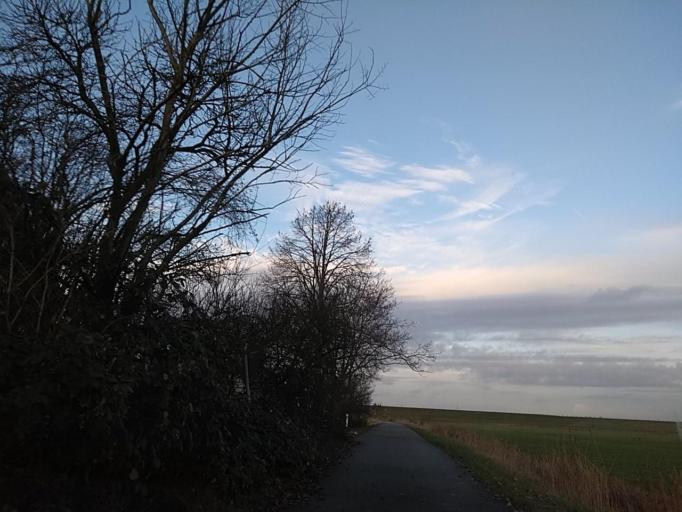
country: DE
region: Lower Saxony
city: Jemgum
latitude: 53.3116
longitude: 7.2947
